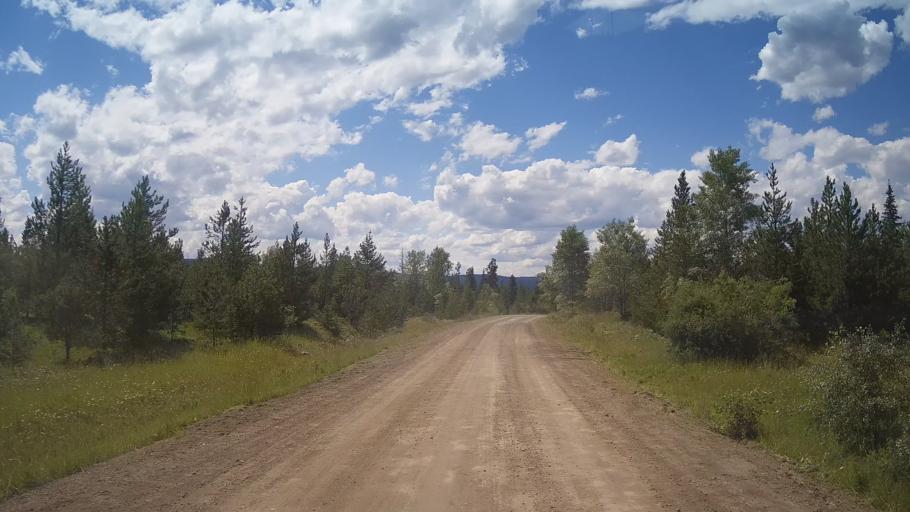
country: CA
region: British Columbia
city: Lillooet
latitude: 51.3397
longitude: -121.9423
